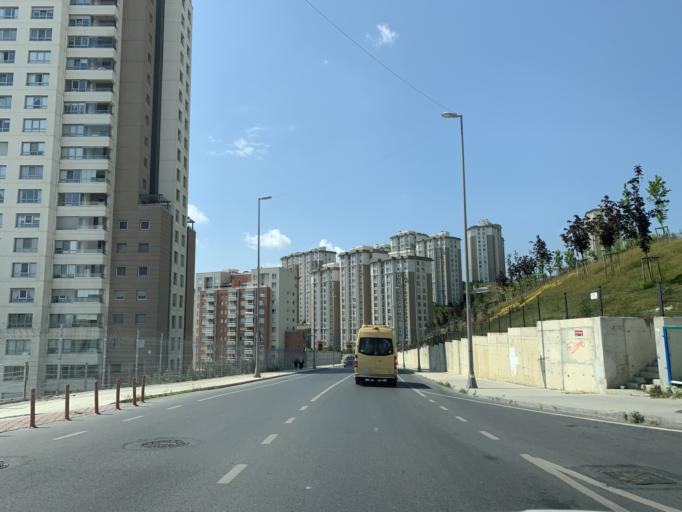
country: TR
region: Istanbul
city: Esenyurt
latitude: 41.0778
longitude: 28.6938
